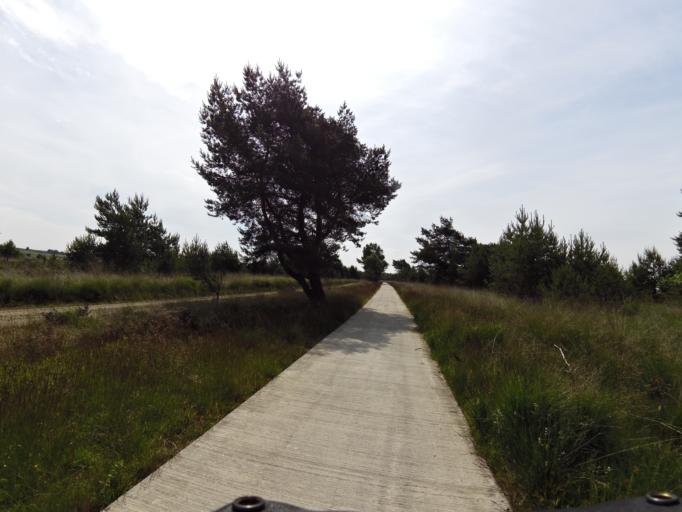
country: NL
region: Gelderland
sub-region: Gemeente Rozendaal
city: Rozendaal
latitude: 52.0460
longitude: 5.9842
